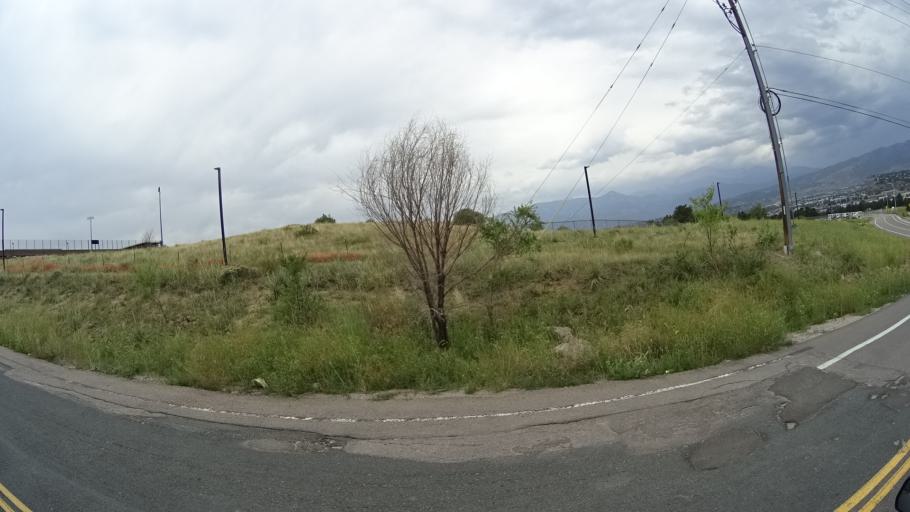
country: US
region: Colorado
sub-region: El Paso County
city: Colorado Springs
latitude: 38.8996
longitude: -104.8077
